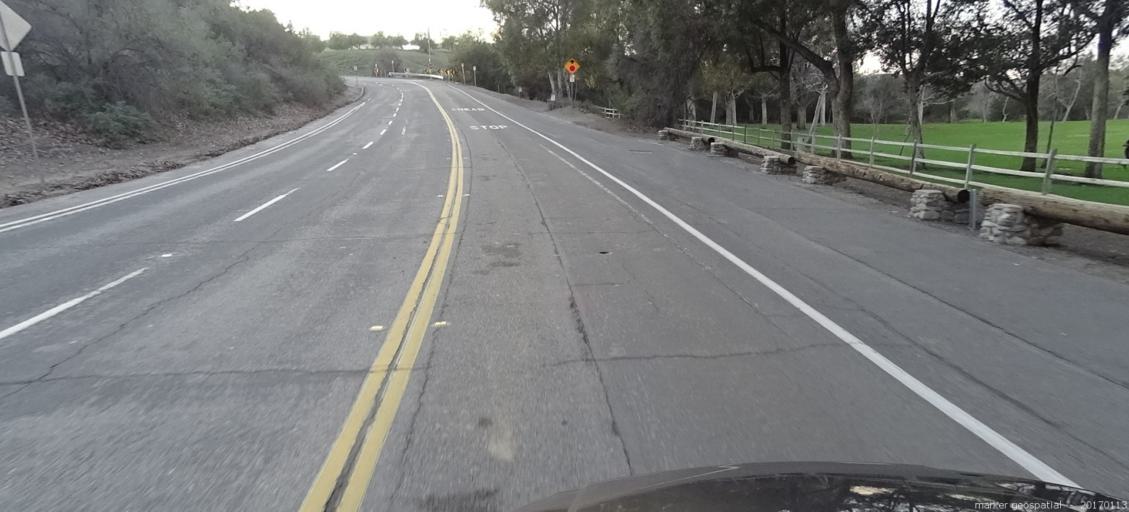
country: US
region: California
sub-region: Orange County
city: North Tustin
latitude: 33.7965
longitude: -117.7592
